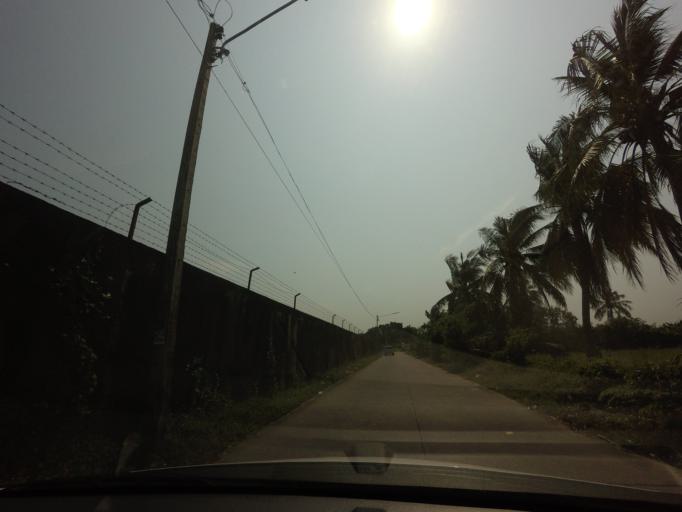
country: TH
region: Nakhon Pathom
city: Sam Phran
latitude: 13.7366
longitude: 100.2647
